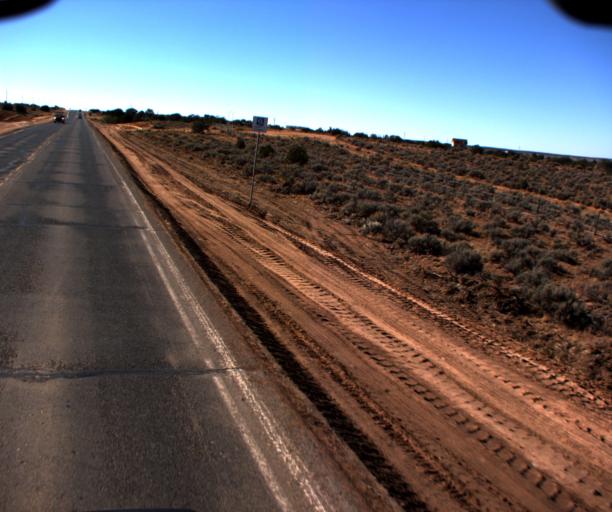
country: US
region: Arizona
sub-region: Apache County
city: Ganado
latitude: 35.7113
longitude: -109.5041
